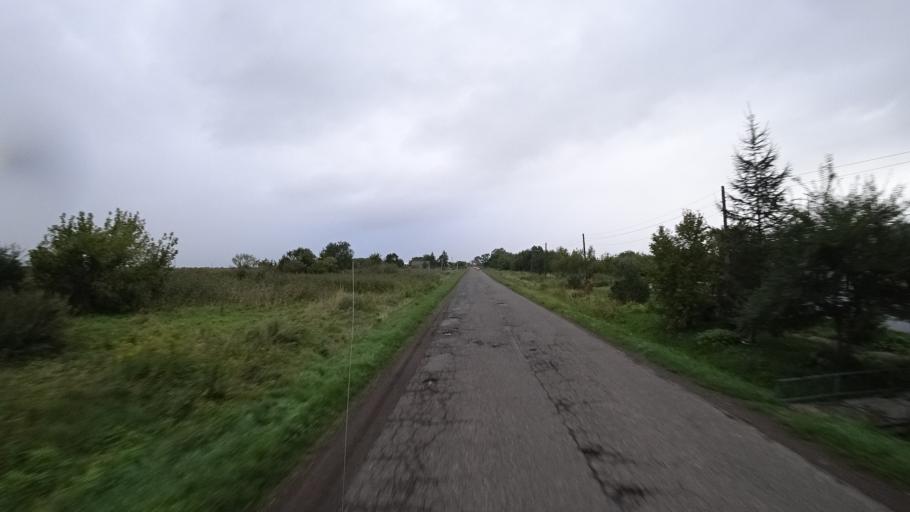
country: RU
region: Primorskiy
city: Chernigovka
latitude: 44.3955
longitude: 132.5281
